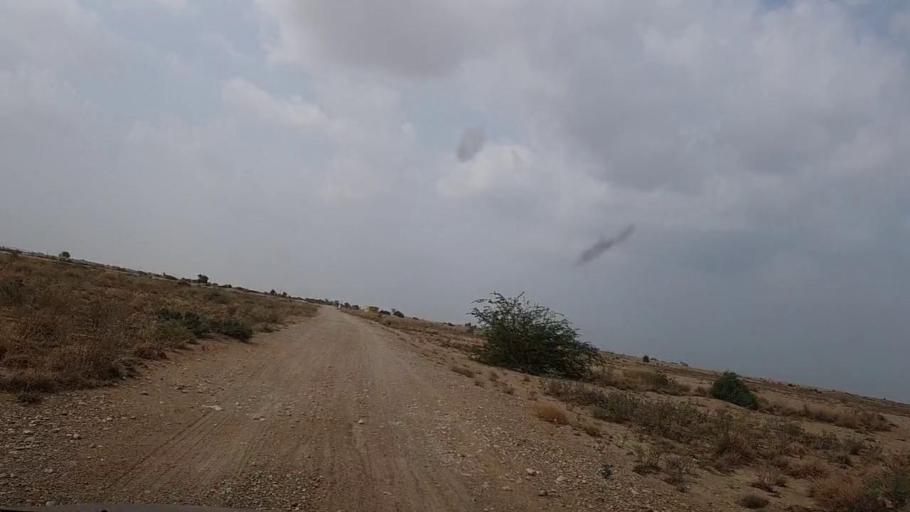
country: PK
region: Sindh
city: Kotri
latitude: 25.2837
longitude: 68.2301
